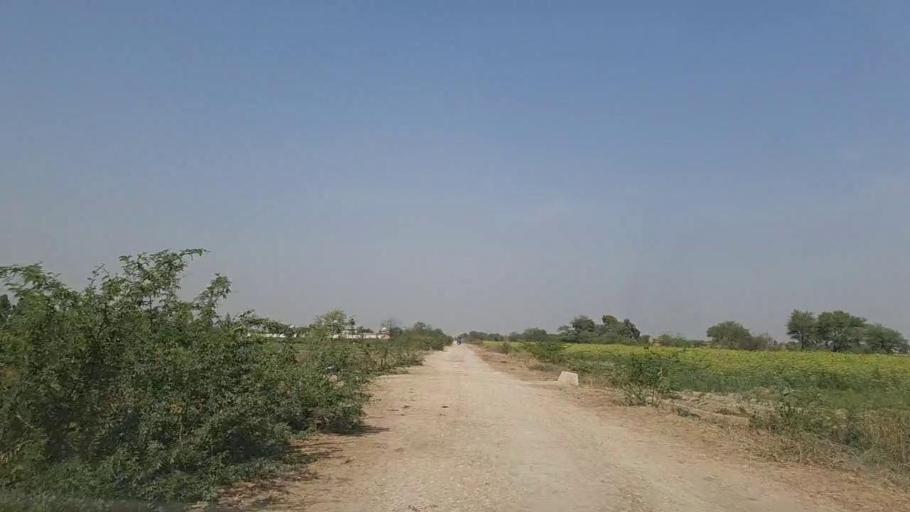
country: PK
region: Sindh
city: Samaro
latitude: 25.2633
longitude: 69.3947
